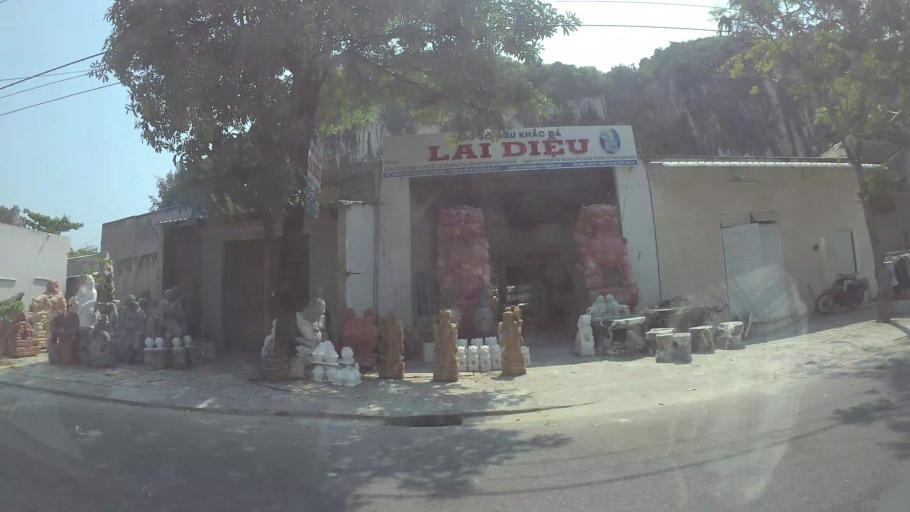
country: VN
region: Da Nang
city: Ngu Hanh Son
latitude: 16.0008
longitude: 108.2621
